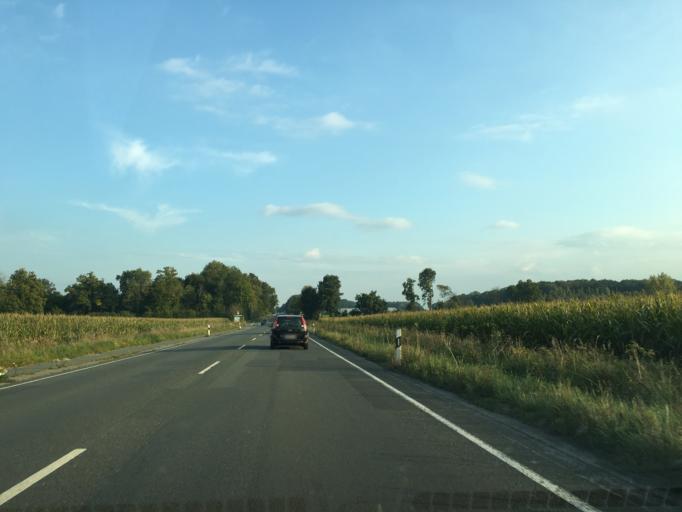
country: DE
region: North Rhine-Westphalia
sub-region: Regierungsbezirk Munster
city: Altenberge
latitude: 52.0289
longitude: 7.4876
